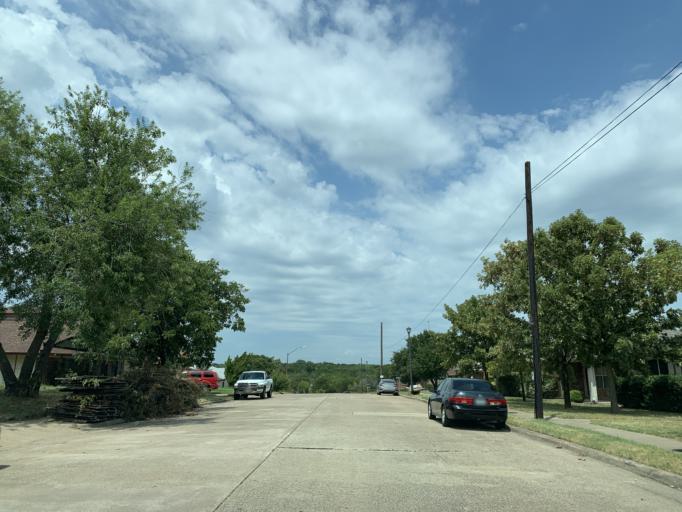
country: US
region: Texas
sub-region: Dallas County
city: DeSoto
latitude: 32.6609
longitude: -96.8122
